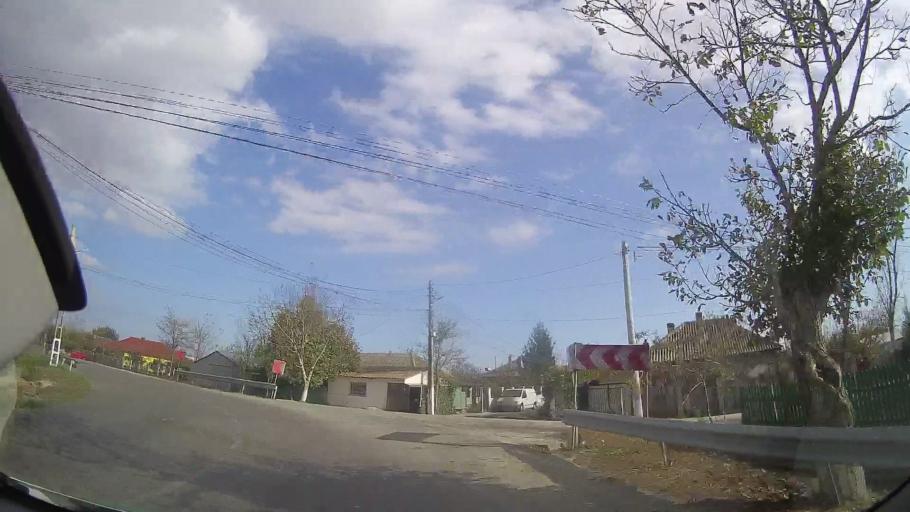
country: RO
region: Constanta
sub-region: Comuna Pecineaga
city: Pecineaga
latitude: 43.8949
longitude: 28.5099
